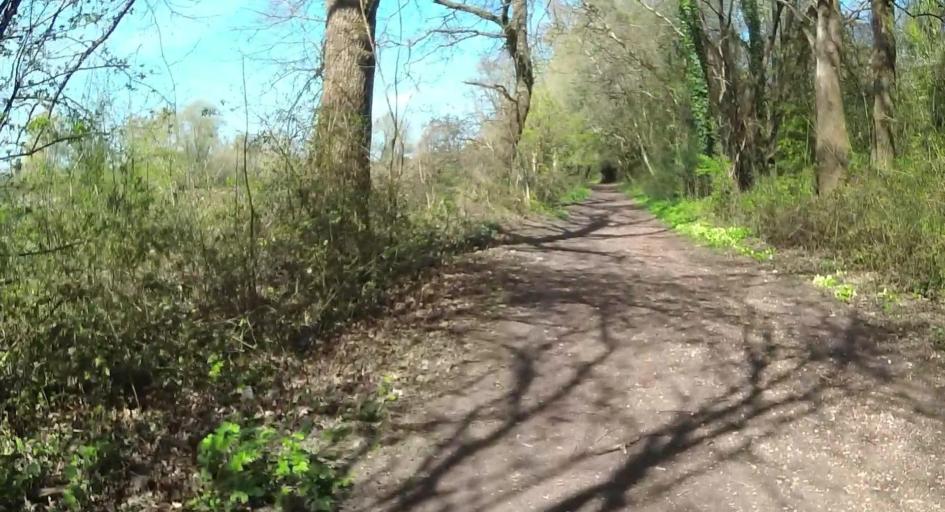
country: GB
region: England
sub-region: Hampshire
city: Romsey
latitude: 51.0786
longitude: -1.5033
